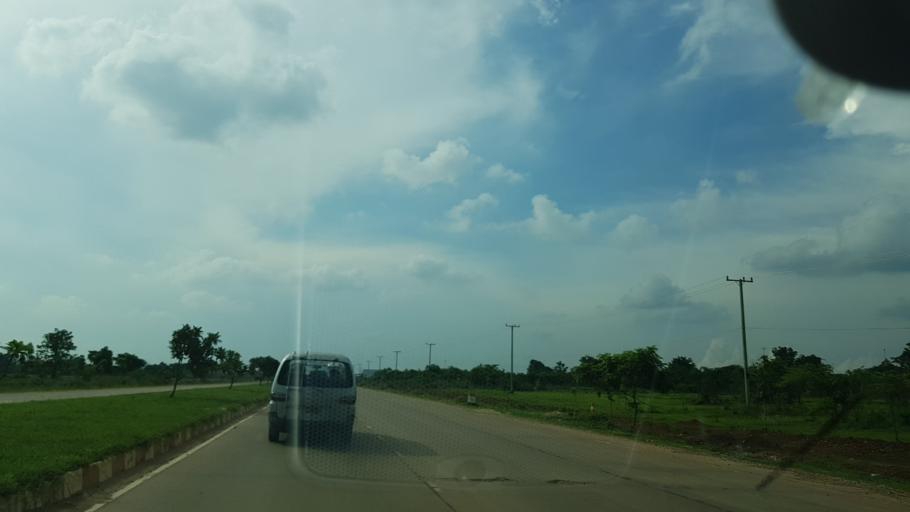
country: LA
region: Vientiane
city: Vientiane
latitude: 17.9922
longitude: 102.7124
